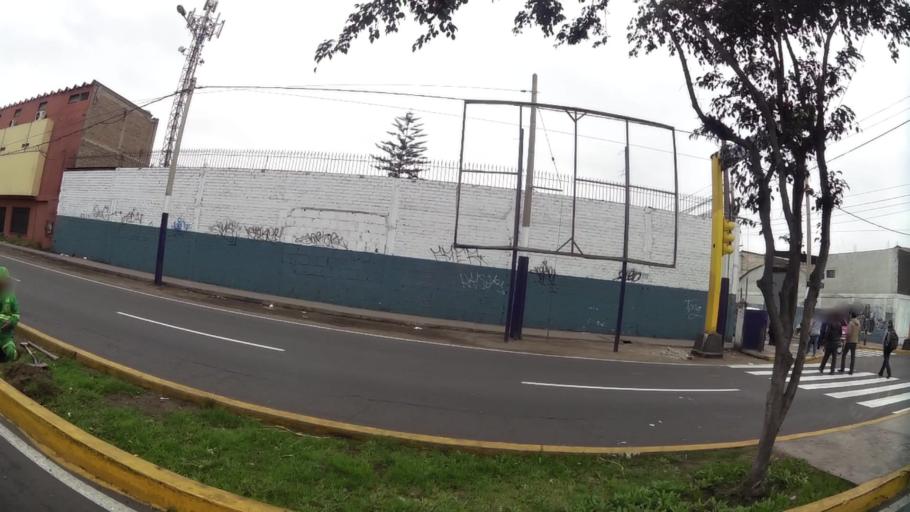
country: PE
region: Lima
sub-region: Lima
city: Surco
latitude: -12.1926
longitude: -77.0081
